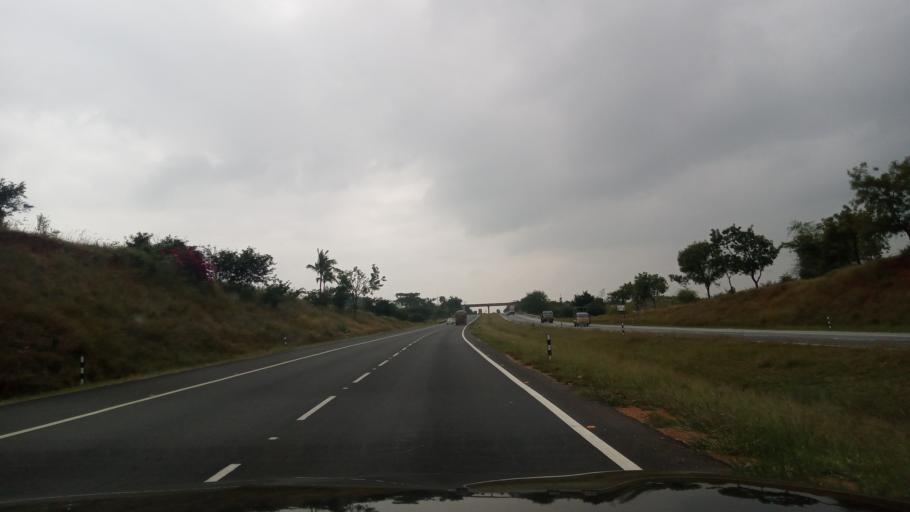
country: IN
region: Karnataka
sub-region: Bangalore Urban
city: Bangalore
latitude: 12.9760
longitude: 77.4713
